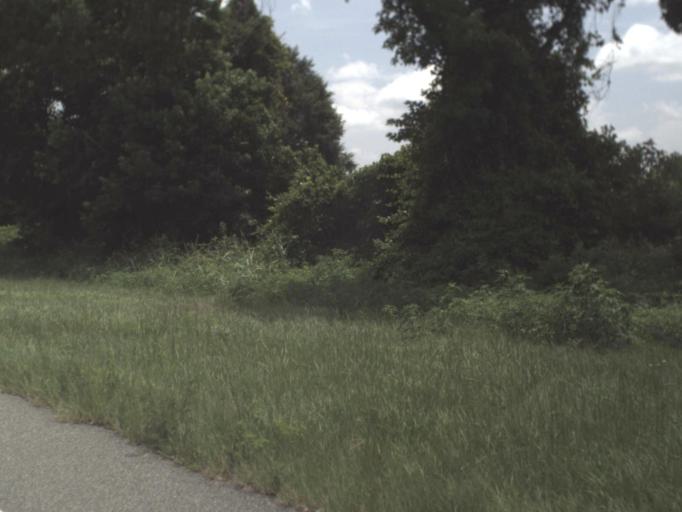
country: US
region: Florida
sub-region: Madison County
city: Madison
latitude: 30.4759
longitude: -83.5593
